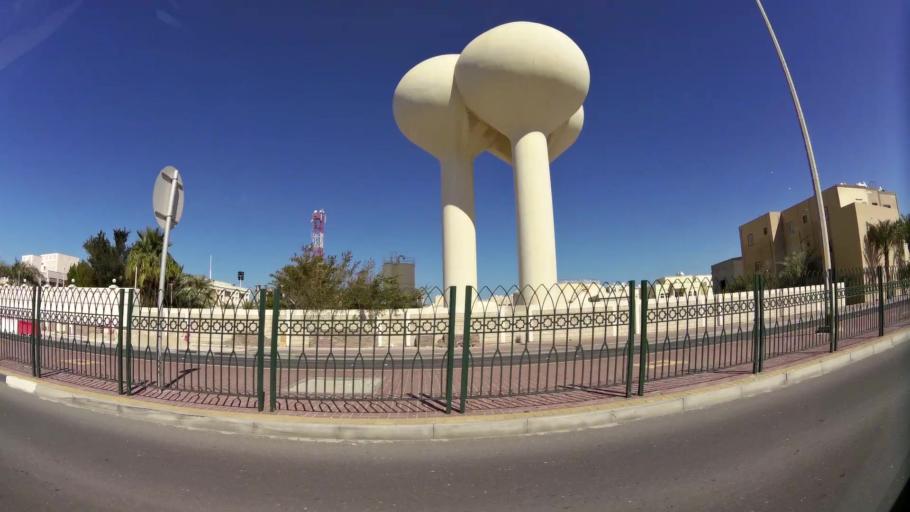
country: BH
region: Muharraq
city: Al Hadd
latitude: 26.2501
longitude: 50.6517
